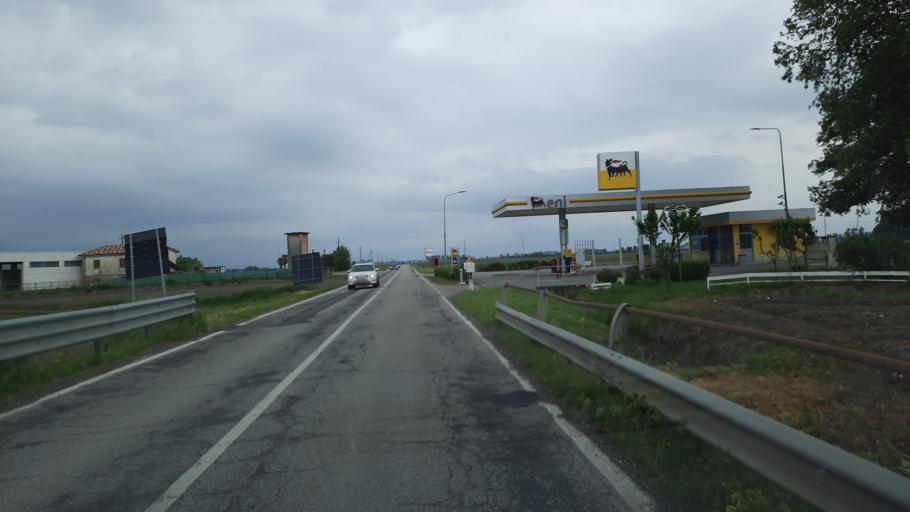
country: IT
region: Lombardy
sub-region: Provincia di Pavia
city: Robbio
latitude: 45.2801
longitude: 8.6039
